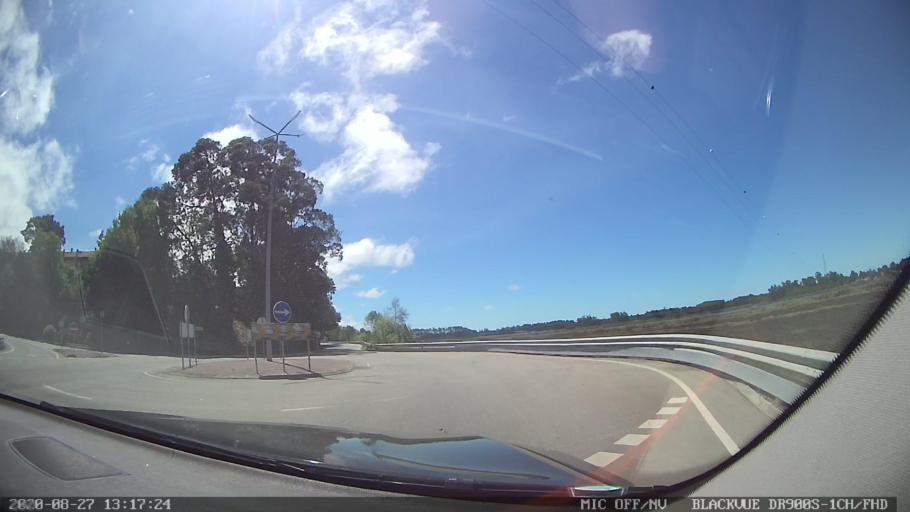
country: PT
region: Aveiro
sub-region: Ilhavo
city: Ilhavo
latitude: 40.5819
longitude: -8.6809
